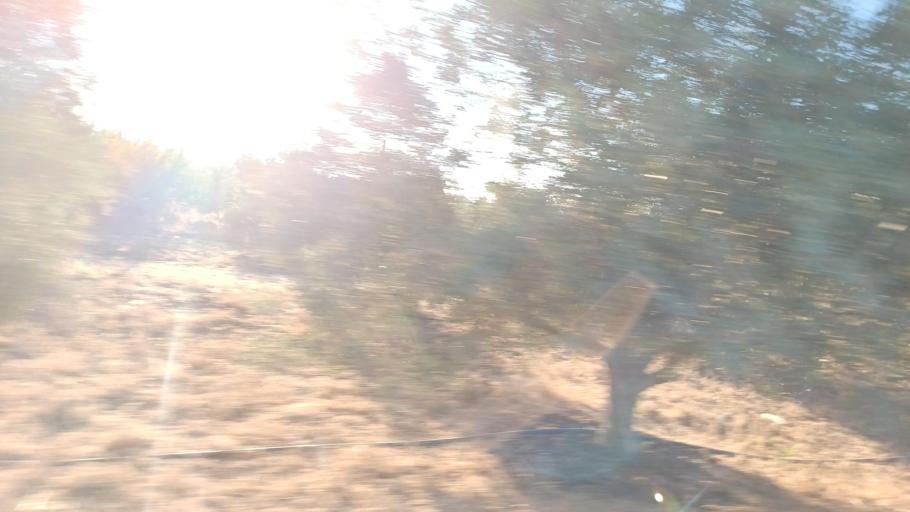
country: CY
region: Ammochostos
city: Achna
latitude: 35.0250
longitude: 33.7938
